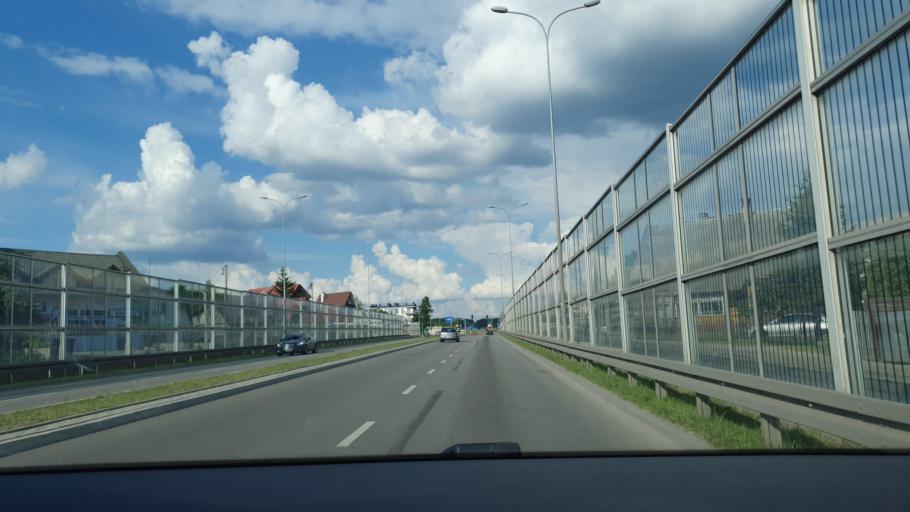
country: PL
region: Podlasie
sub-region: Bialystok
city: Bialystok
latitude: 53.1230
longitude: 23.2049
